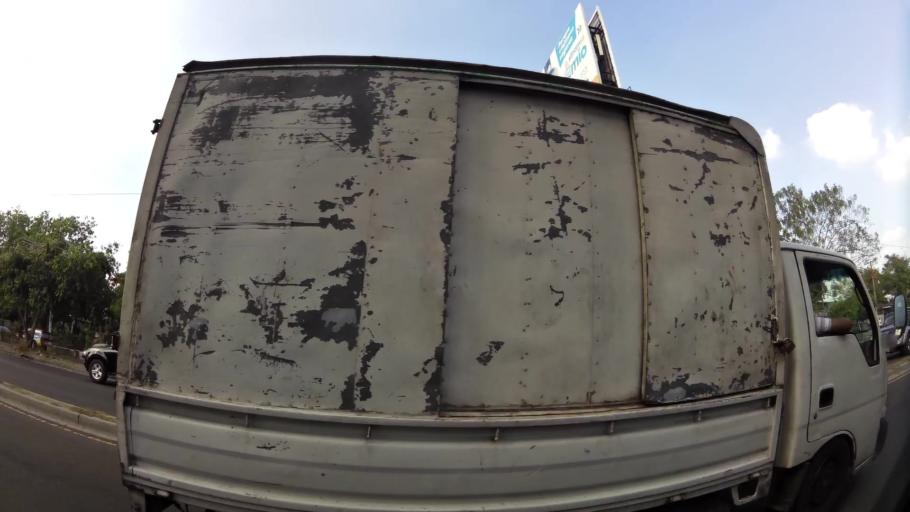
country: SV
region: San Salvador
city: Soyapango
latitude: 13.7173
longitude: -89.1369
